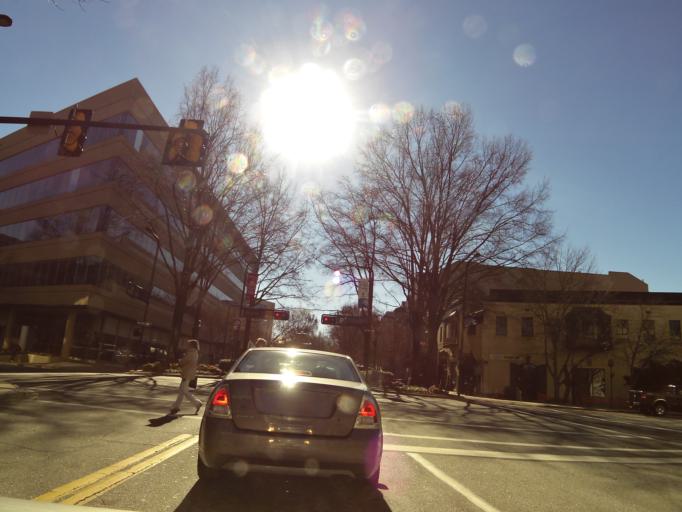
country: US
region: South Carolina
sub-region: Greenville County
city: Greenville
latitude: 34.8542
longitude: -82.3975
